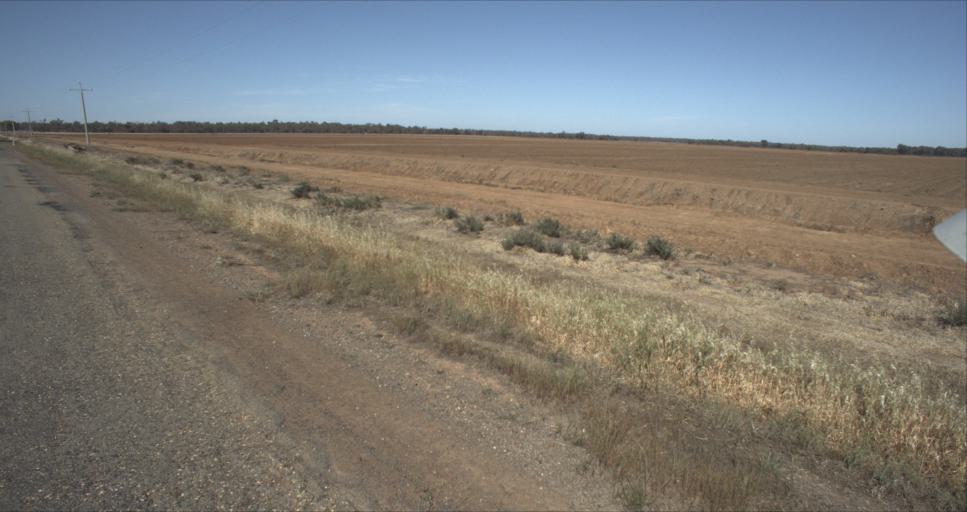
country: AU
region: New South Wales
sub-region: Leeton
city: Leeton
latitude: -34.5969
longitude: 146.2585
